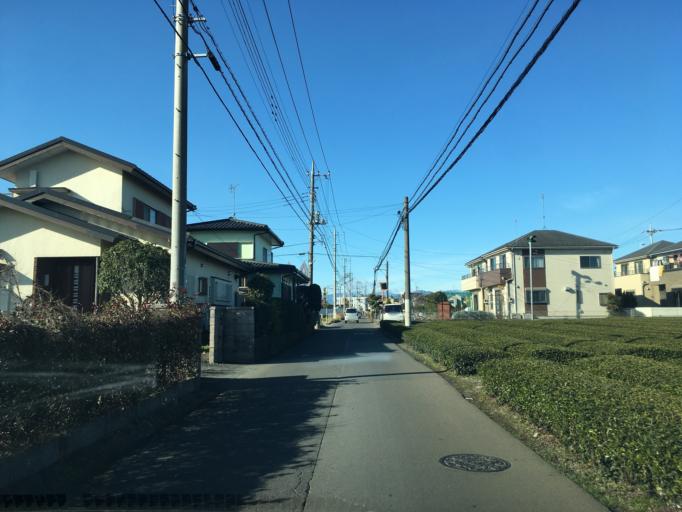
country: JP
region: Saitama
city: Tokorozawa
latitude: 35.8001
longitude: 139.4172
